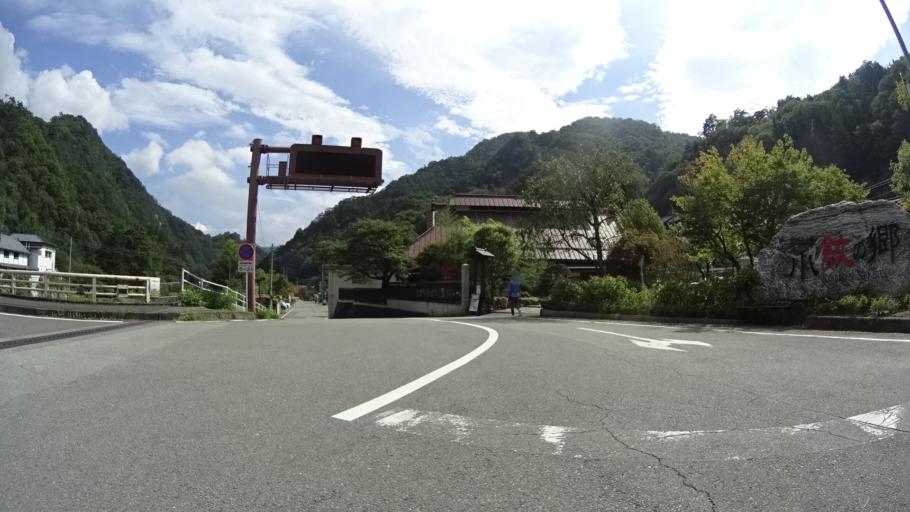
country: JP
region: Yamanashi
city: Kofu-shi
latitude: 35.7550
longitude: 138.5642
